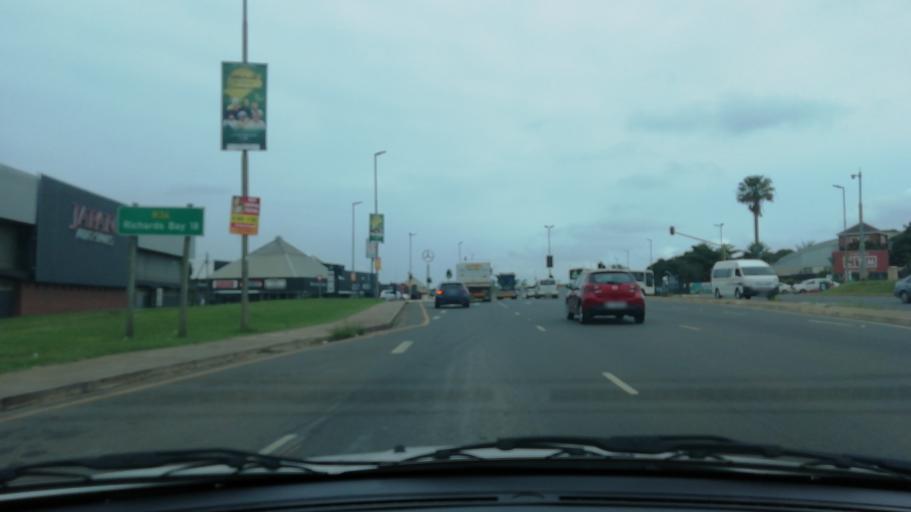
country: ZA
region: KwaZulu-Natal
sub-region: uThungulu District Municipality
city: Empangeni
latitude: -28.7648
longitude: 31.9087
